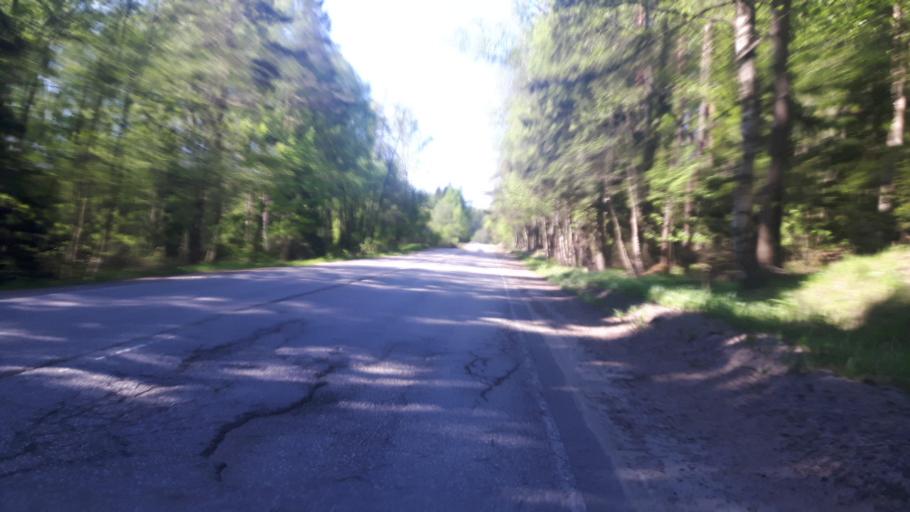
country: RU
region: Leningrad
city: Vyborg
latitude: 60.6410
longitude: 28.7403
